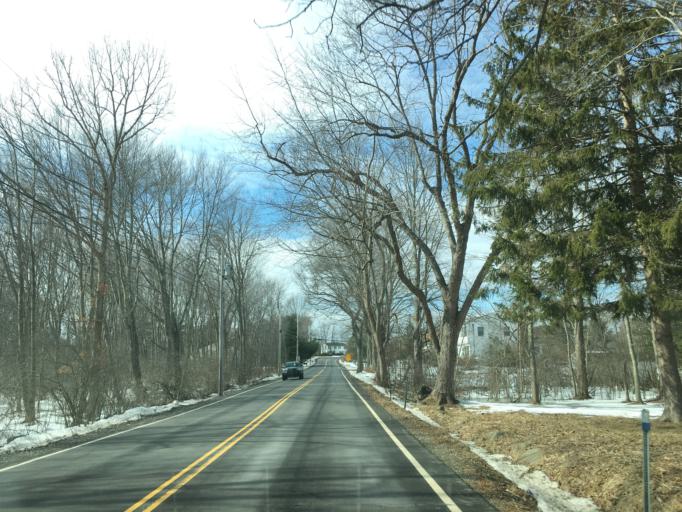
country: US
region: New Hampshire
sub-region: Rockingham County
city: North Hampton
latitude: 42.9911
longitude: -70.8811
